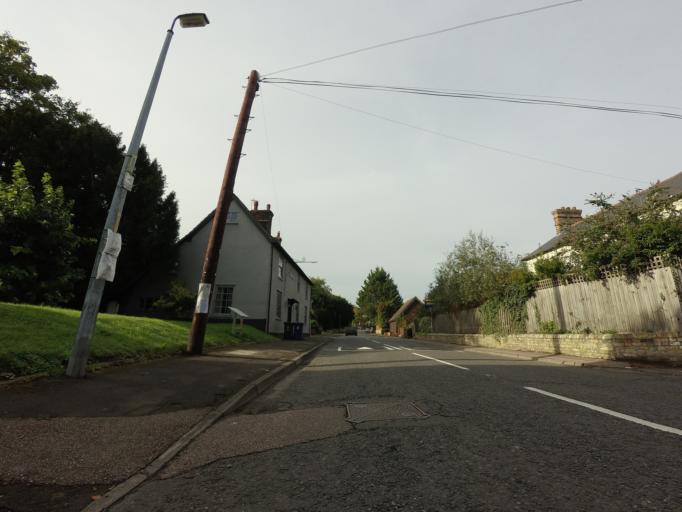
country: GB
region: England
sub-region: Cambridgeshire
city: Harston
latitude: 52.0935
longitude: 0.0746
